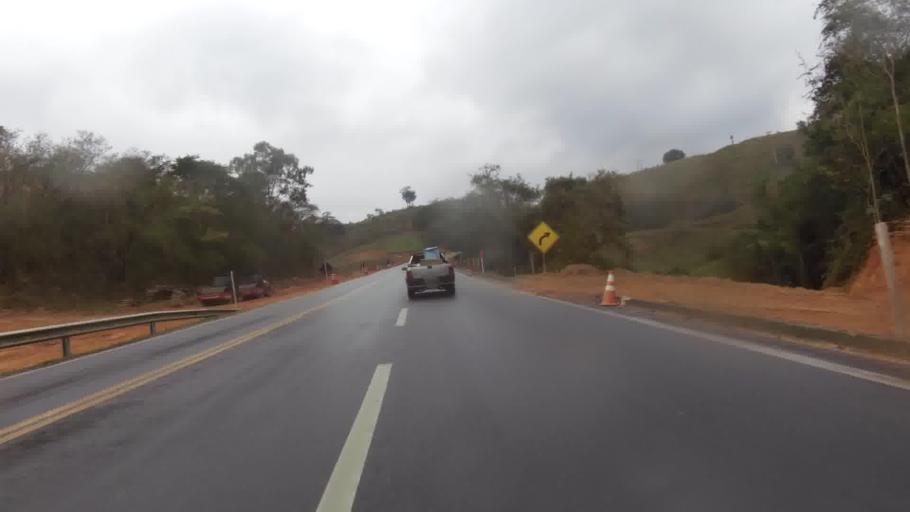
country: BR
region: Espirito Santo
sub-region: Rio Novo Do Sul
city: Rio Novo do Sul
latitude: -20.9005
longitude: -41.0154
